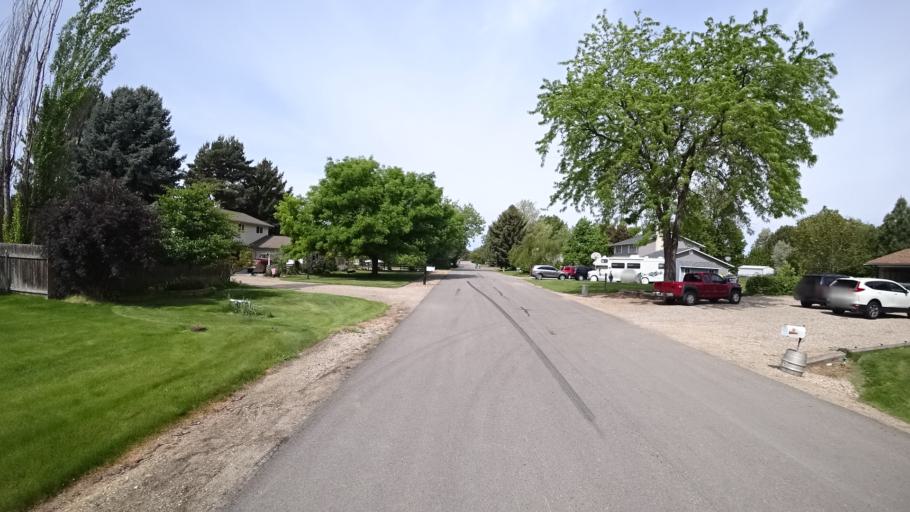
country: US
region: Idaho
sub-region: Ada County
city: Meridian
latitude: 43.5800
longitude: -116.3195
